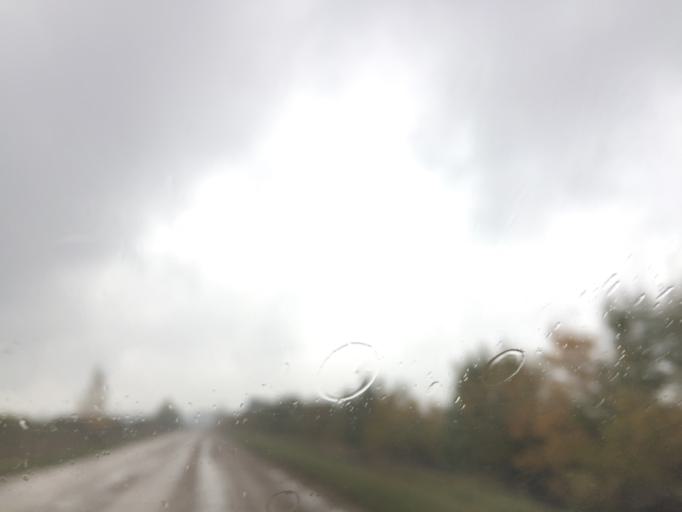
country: LV
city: Tireli
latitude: 56.7271
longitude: 23.5037
